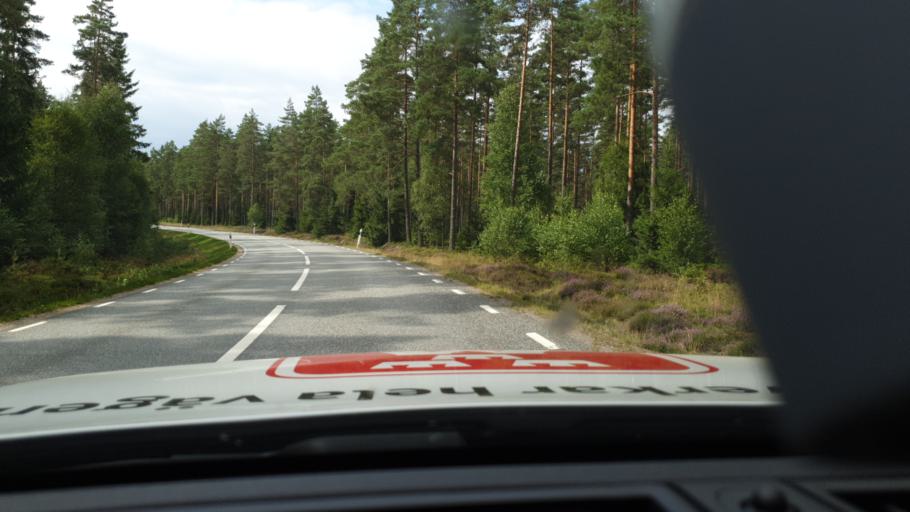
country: SE
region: Joenkoeping
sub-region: Vaggeryds Kommun
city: Skillingaryd
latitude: 57.3819
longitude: 13.9756
